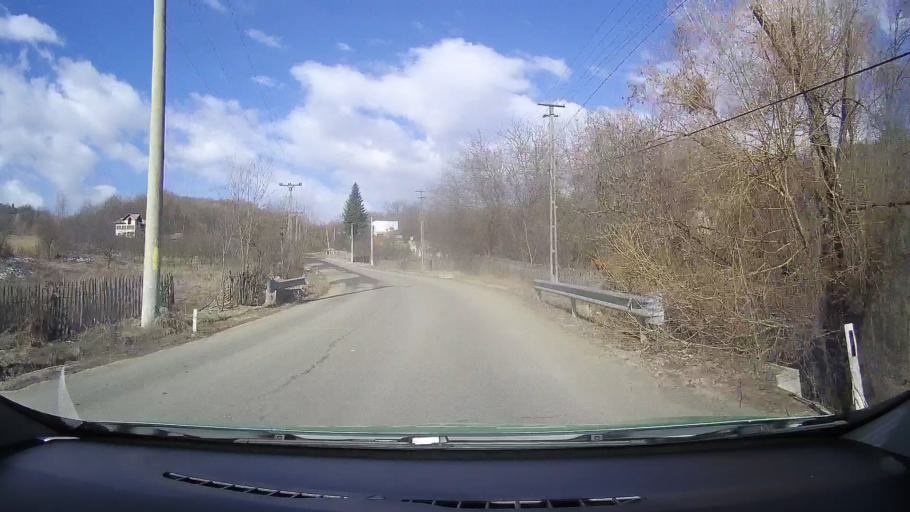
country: RO
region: Dambovita
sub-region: Oras Pucioasa
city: Glodeni
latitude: 45.0909
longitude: 25.4789
